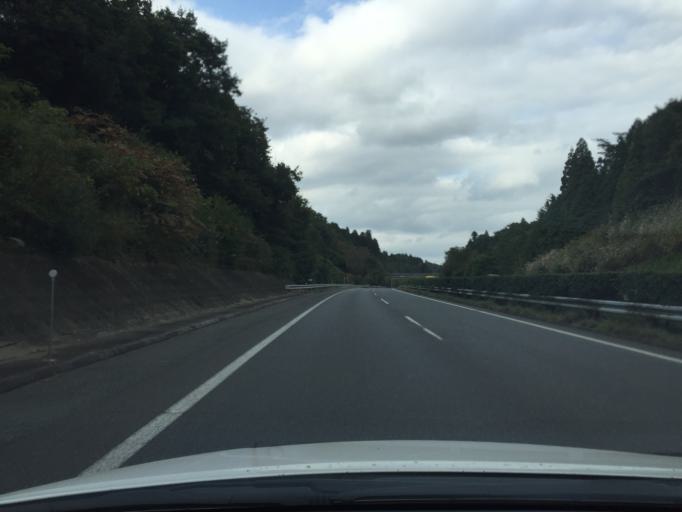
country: JP
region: Fukushima
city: Iwaki
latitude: 36.9450
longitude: 140.7726
